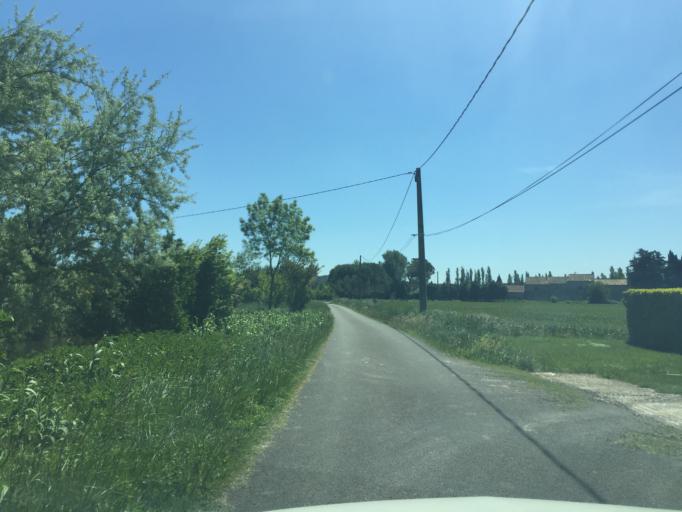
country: FR
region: Provence-Alpes-Cote d'Azur
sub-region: Departement du Vaucluse
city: Caderousse
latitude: 44.1070
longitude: 4.7866
